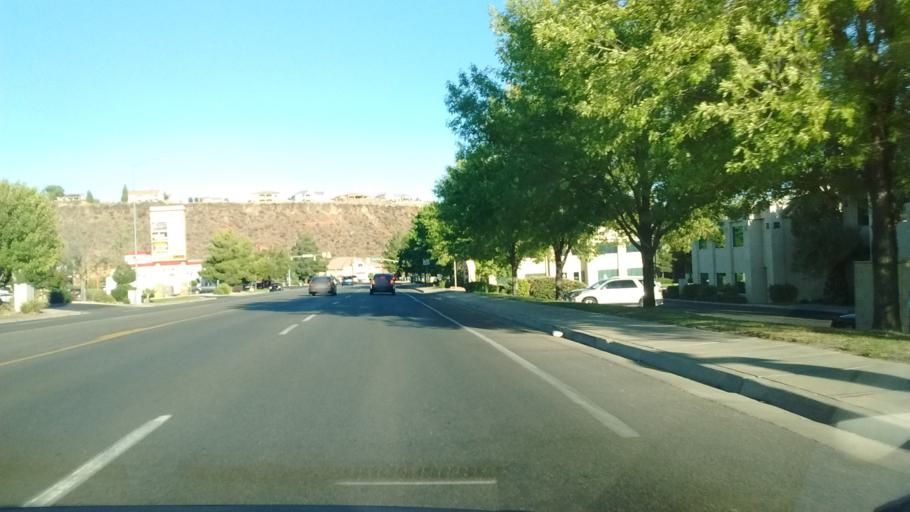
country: US
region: Utah
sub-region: Washington County
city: Saint George
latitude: 37.1064
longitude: -113.5577
